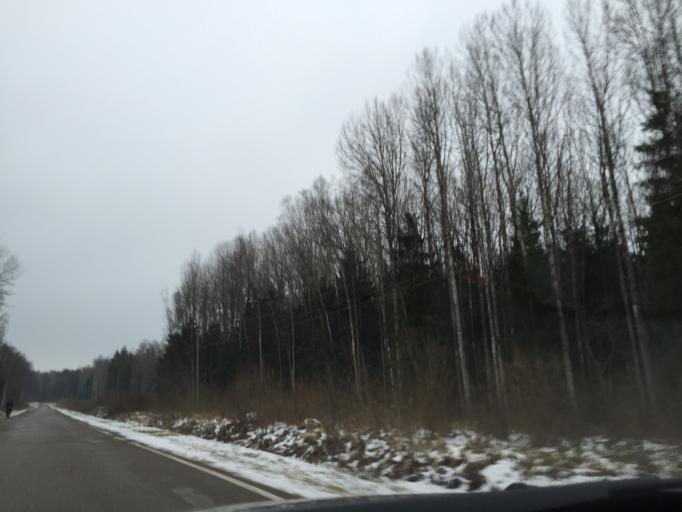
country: LV
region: Saulkrastu
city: Saulkrasti
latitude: 57.4897
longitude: 24.3998
